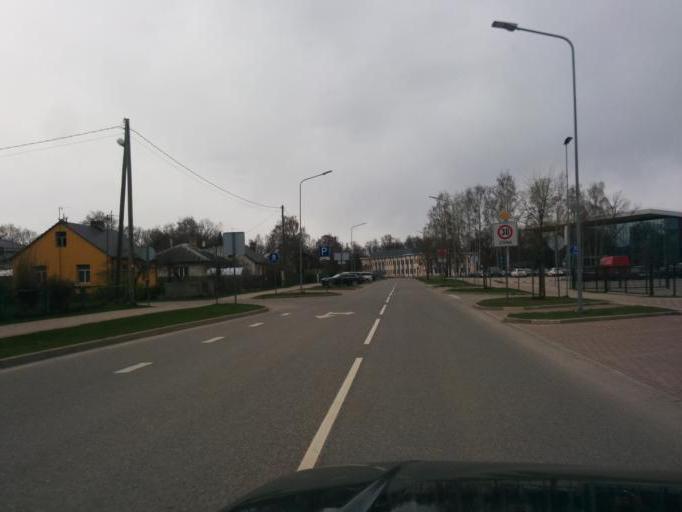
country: LV
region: Jelgava
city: Jelgava
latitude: 56.6594
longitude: 23.7541
